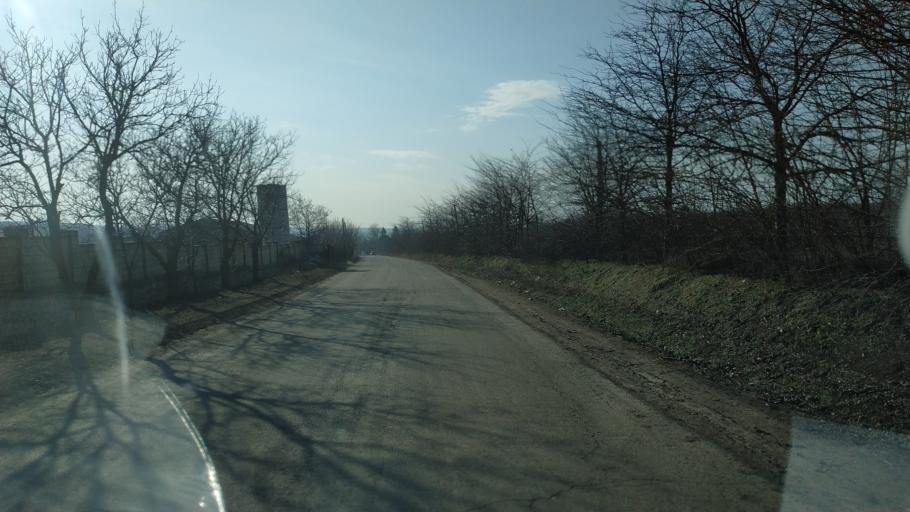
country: MD
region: Chisinau
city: Singera
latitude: 46.8437
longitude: 29.0253
